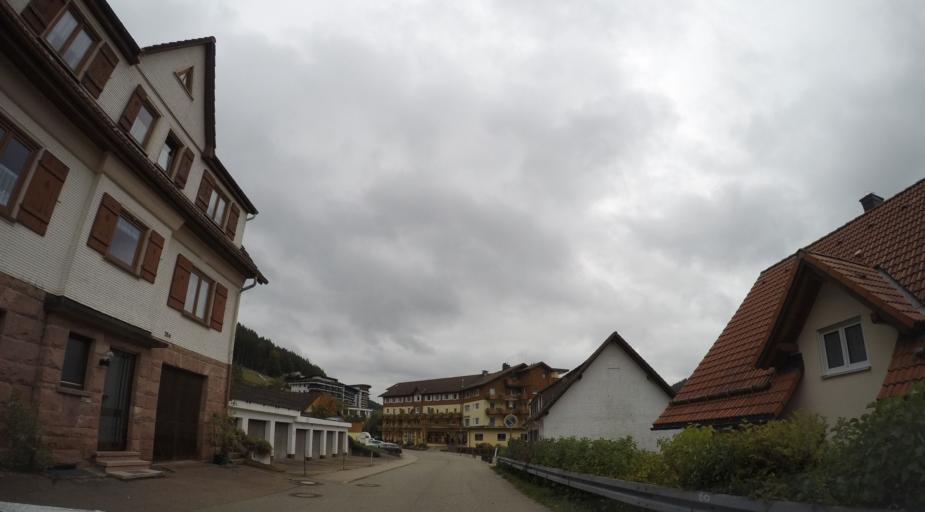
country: DE
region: Baden-Wuerttemberg
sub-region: Karlsruhe Region
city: Baiersbronn
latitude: 48.5391
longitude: 8.3561
